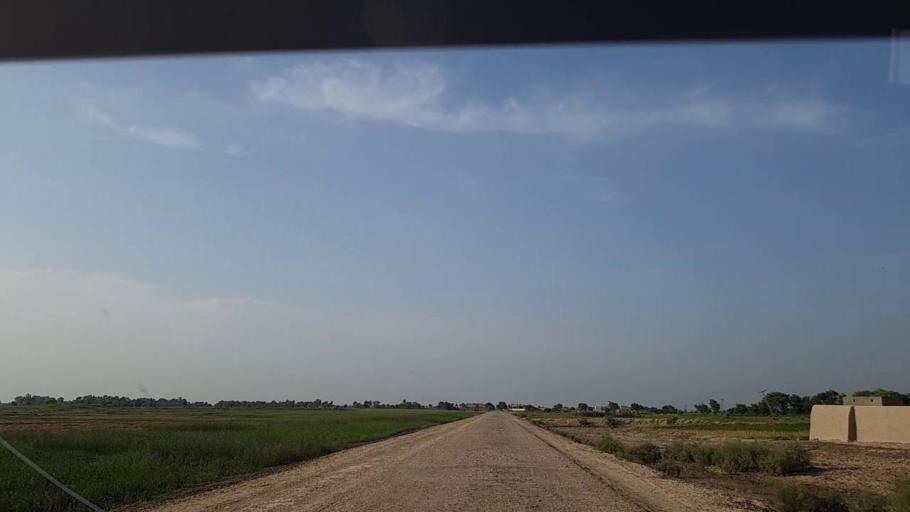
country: PK
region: Sindh
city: Khanpur
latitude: 27.8317
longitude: 69.3741
